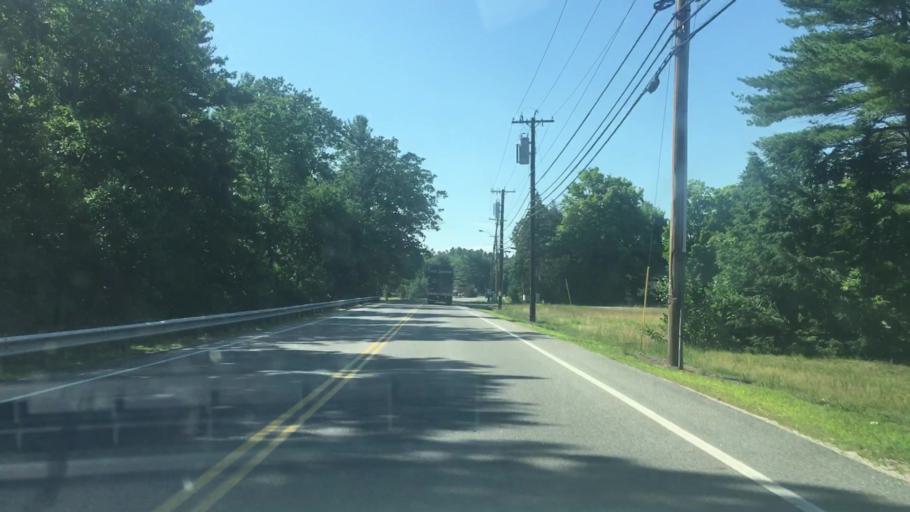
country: US
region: Maine
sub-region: York County
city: Biddeford
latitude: 43.5544
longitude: -70.4953
